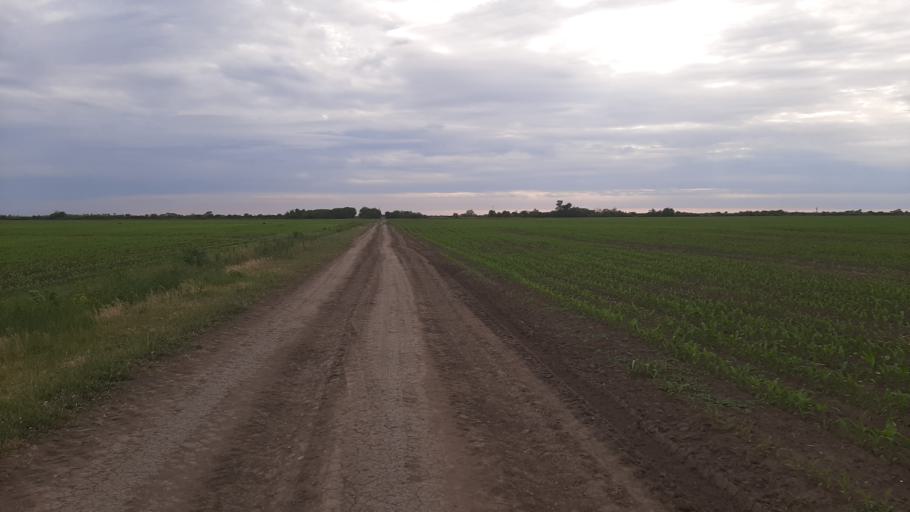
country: HU
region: Csongrad
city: Deszk
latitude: 46.1726
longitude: 20.2132
